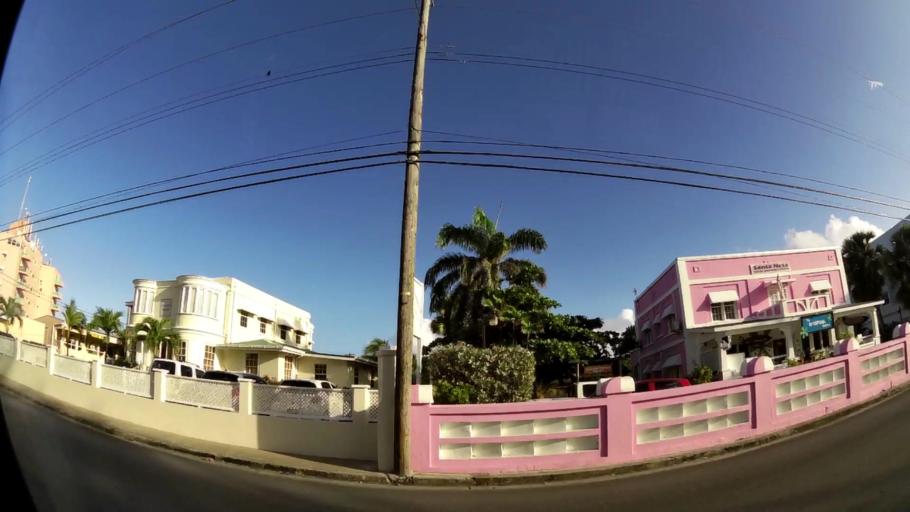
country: BB
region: Saint Michael
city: Bridgetown
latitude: 13.0741
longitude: -59.5970
